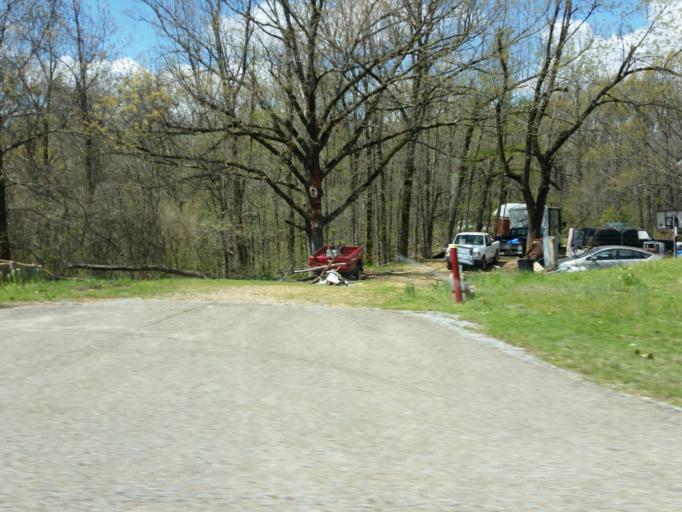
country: US
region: Arkansas
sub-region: Craighead County
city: Bono
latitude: 35.9765
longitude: -90.7129
